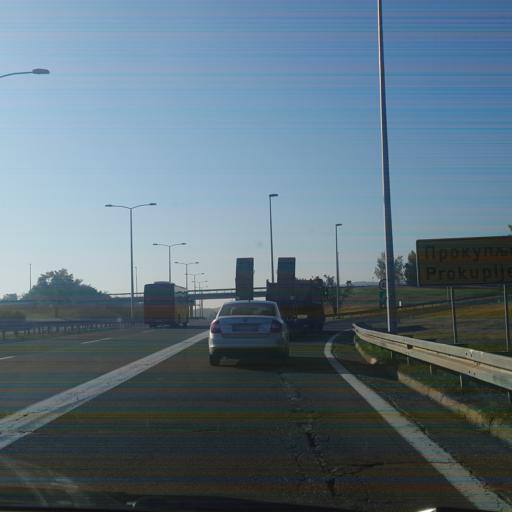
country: RS
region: Central Serbia
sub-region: Nisavski Okrug
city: Merosina
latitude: 43.2818
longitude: 21.8014
